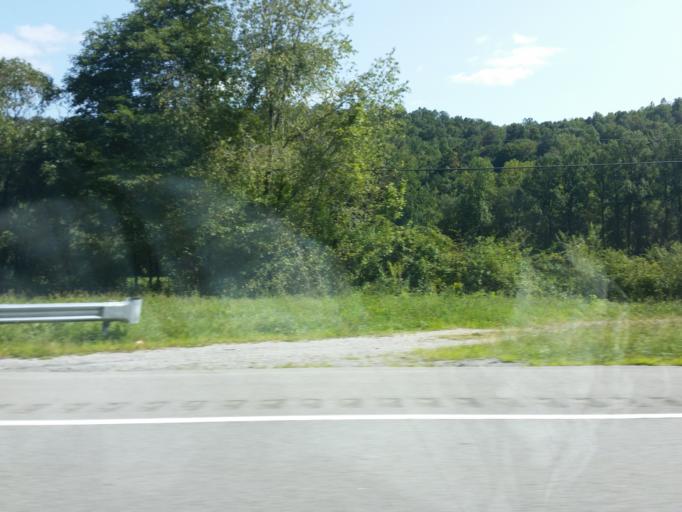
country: US
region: Kentucky
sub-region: Bell County
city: Pineville
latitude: 36.7853
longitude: -83.5592
